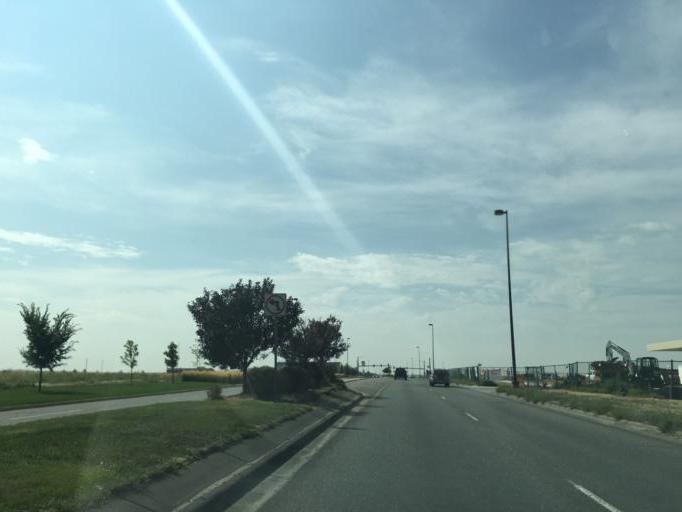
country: US
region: Colorado
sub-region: Adams County
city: Aurora
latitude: 39.8159
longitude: -104.7721
